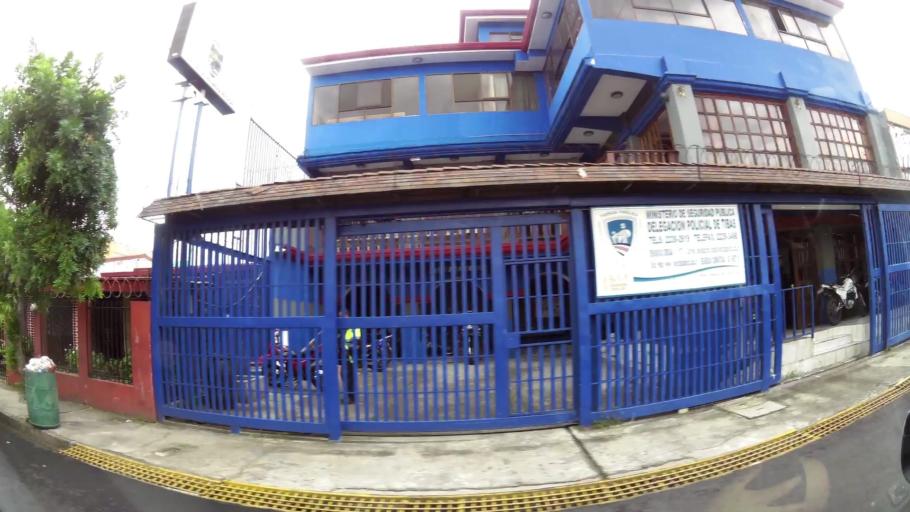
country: CR
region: San Jose
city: San Juan
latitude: 9.9593
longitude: -84.0776
